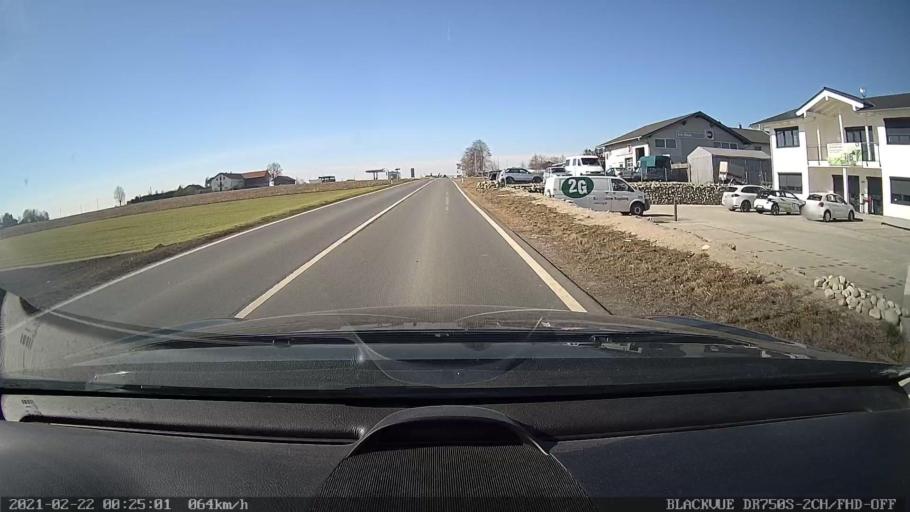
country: DE
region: Bavaria
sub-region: Upper Bavaria
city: Griesstatt
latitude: 47.9891
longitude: 12.1806
